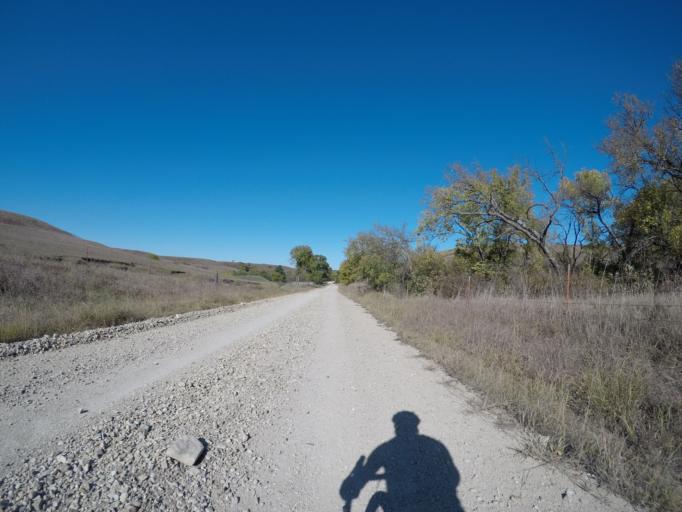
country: US
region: Kansas
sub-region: Wabaunsee County
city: Alma
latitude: 38.9255
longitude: -96.3951
